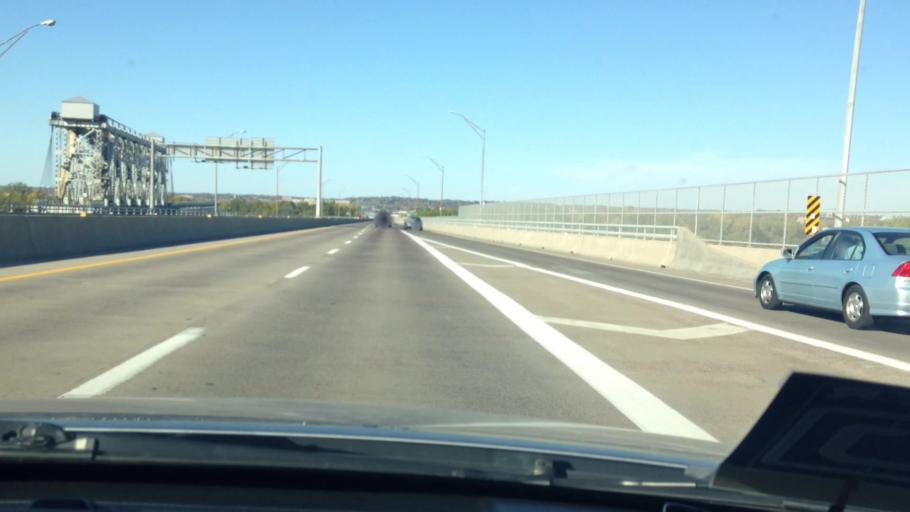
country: US
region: Missouri
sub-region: Jackson County
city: Kansas City
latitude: 39.1132
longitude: -94.5780
